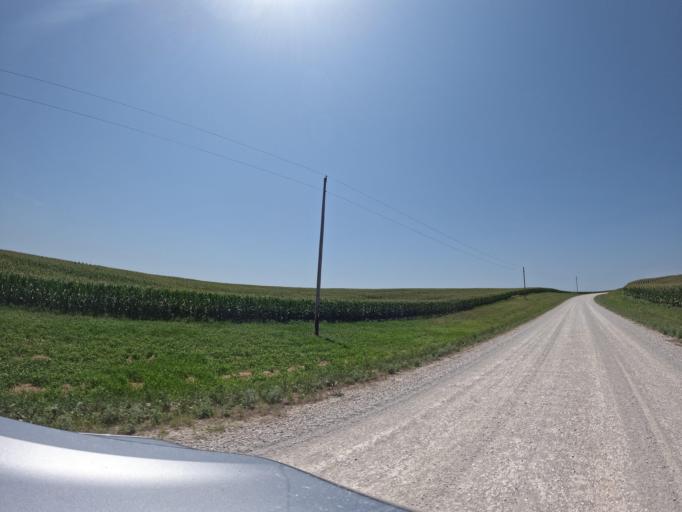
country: US
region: Iowa
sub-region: Henry County
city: Mount Pleasant
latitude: 40.9380
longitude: -91.6325
